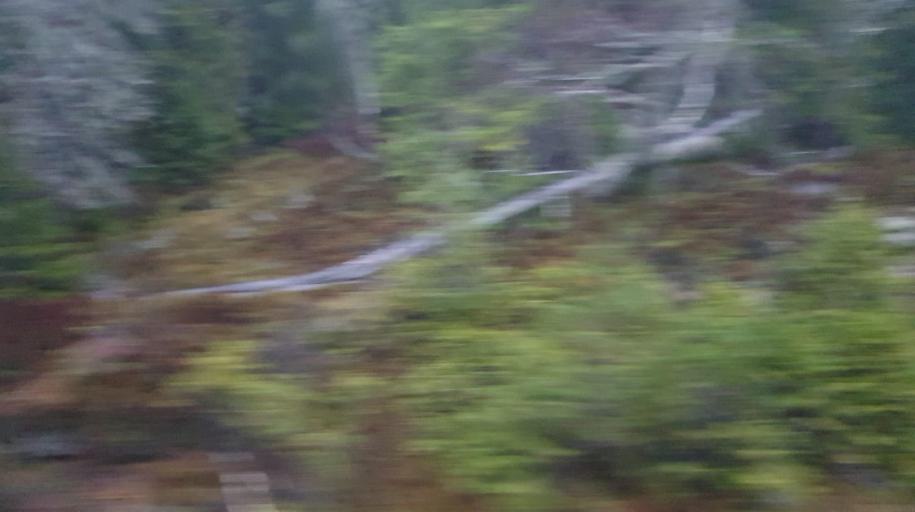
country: NO
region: Buskerud
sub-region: Krodsherad
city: Noresund
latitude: 60.2161
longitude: 9.5445
